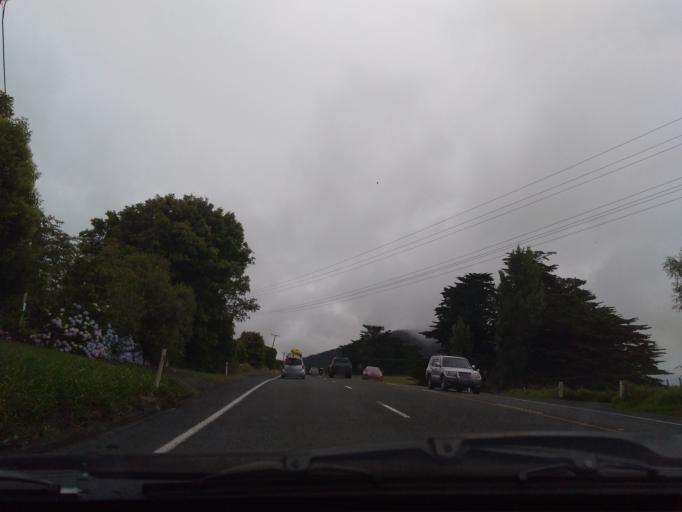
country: NZ
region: Auckland
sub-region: Auckland
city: Wellsford
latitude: -36.1493
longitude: 174.4389
